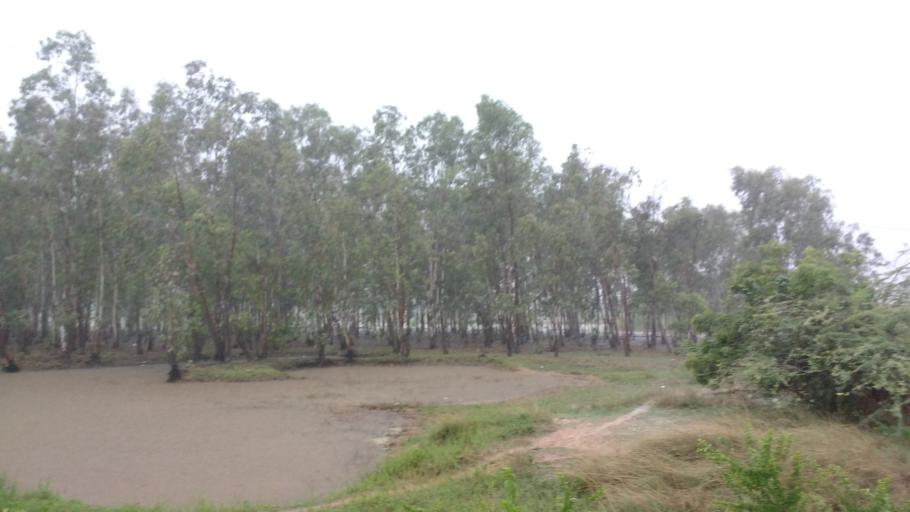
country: IN
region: Tamil Nadu
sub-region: Kancheepuram
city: Sriperumbudur
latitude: 12.9780
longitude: 79.9314
